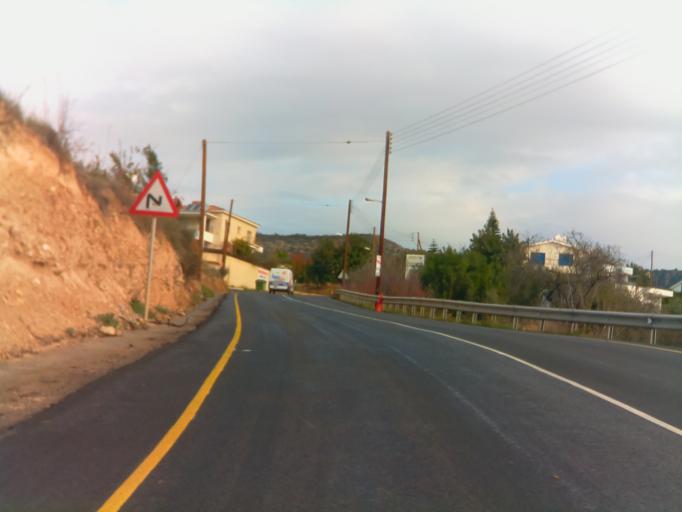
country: CY
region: Pafos
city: Pegeia
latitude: 34.8684
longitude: 32.3780
